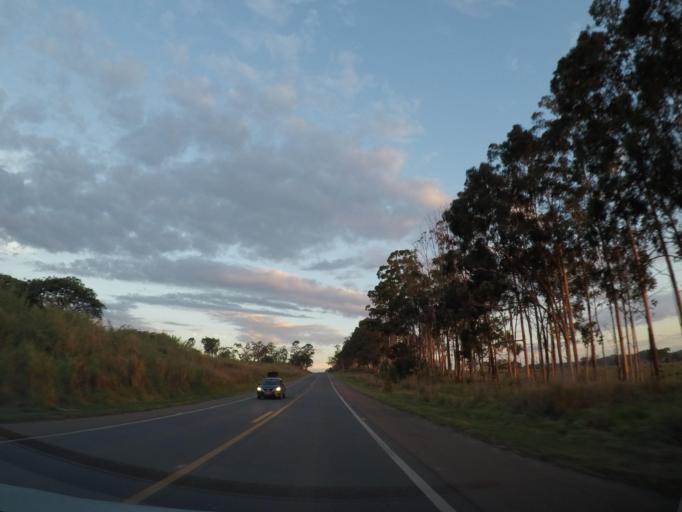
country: BR
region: Sao Paulo
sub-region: Itupeva
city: Itupeva
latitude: -23.0466
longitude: -47.0950
